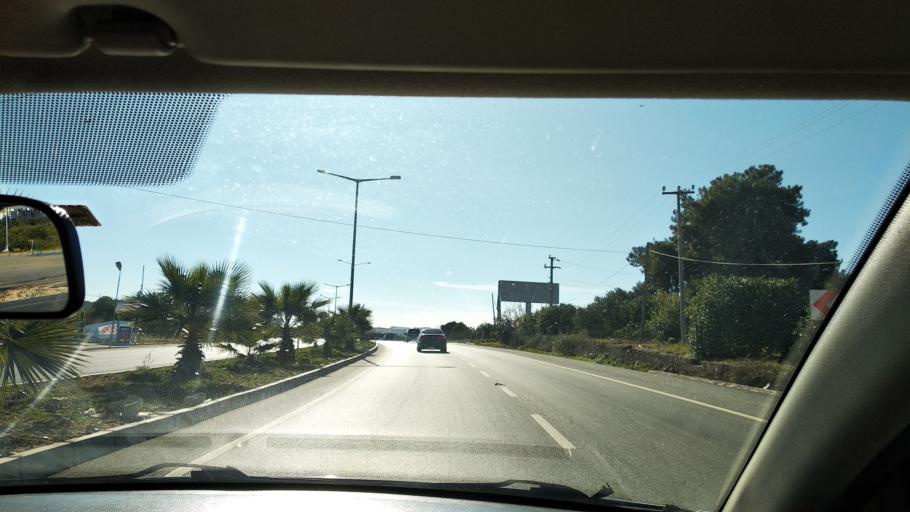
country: TR
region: Mersin
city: Tomuk
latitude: 36.6663
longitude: 34.3995
